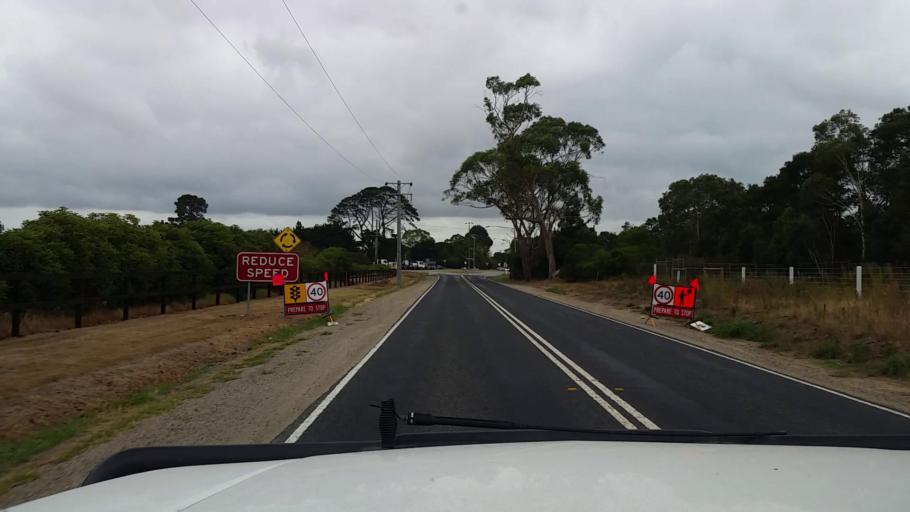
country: AU
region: Victoria
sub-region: Mornington Peninsula
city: Tyabb
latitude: -38.2602
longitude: 145.1456
